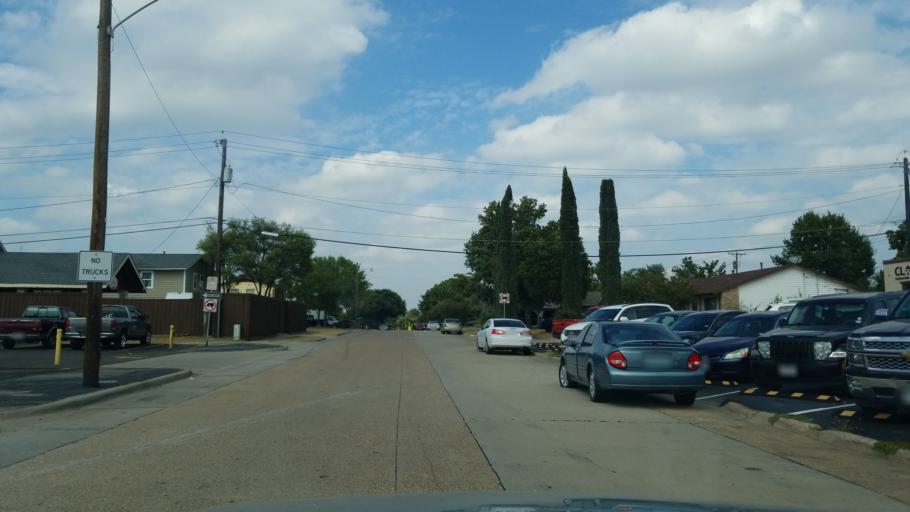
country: US
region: Texas
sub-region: Dallas County
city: Garland
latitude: 32.9101
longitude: -96.6922
